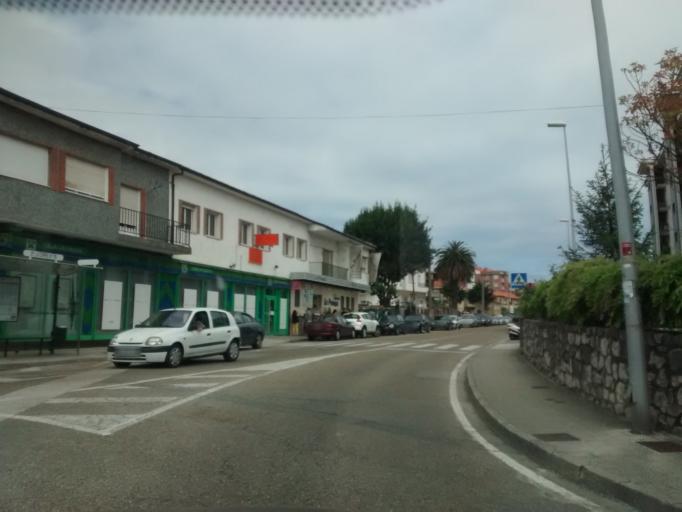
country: ES
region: Cantabria
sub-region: Provincia de Cantabria
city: Santander
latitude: 43.4697
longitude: -3.8248
